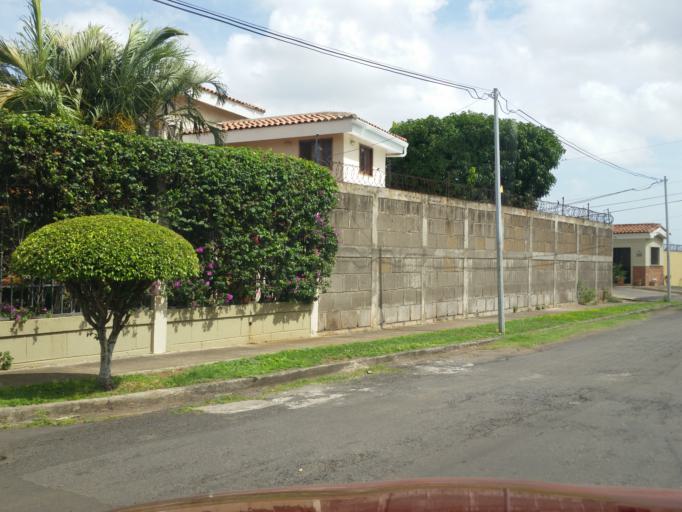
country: NI
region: Managua
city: Managua
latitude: 12.1167
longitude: -86.2801
